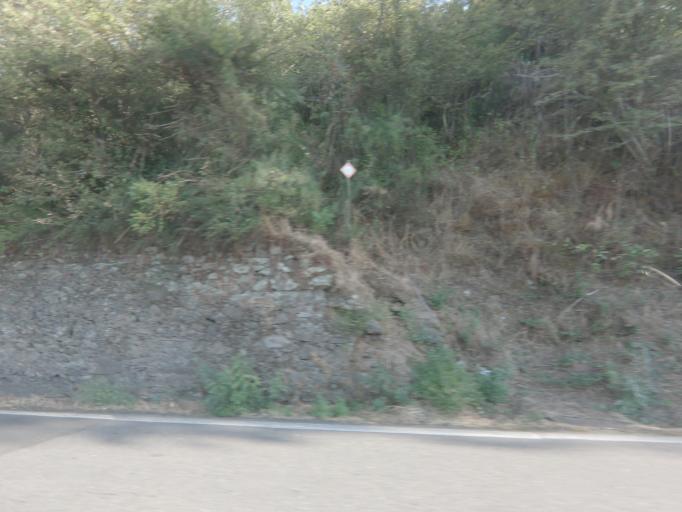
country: PT
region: Vila Real
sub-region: Peso da Regua
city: Peso da Regua
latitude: 41.1516
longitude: -7.7707
